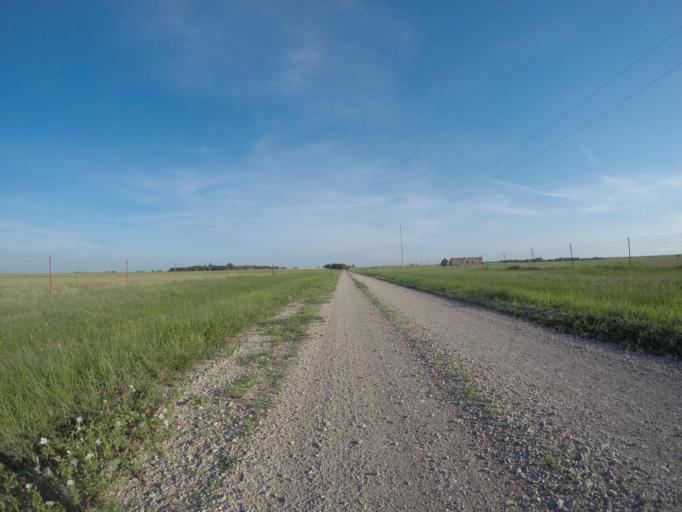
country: US
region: Kansas
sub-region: Wabaunsee County
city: Alma
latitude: 38.9908
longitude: -96.4921
